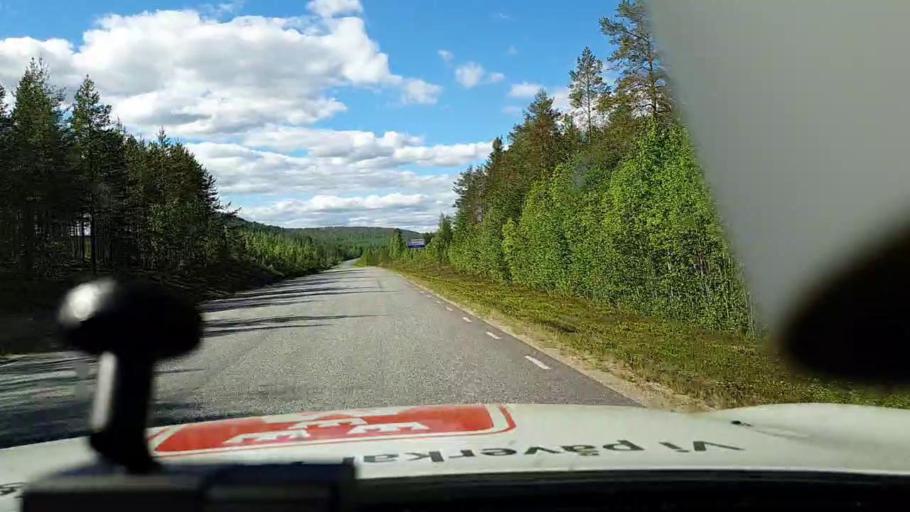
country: FI
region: Lapland
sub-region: Torniolaakso
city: Ylitornio
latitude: 66.2981
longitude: 23.6353
